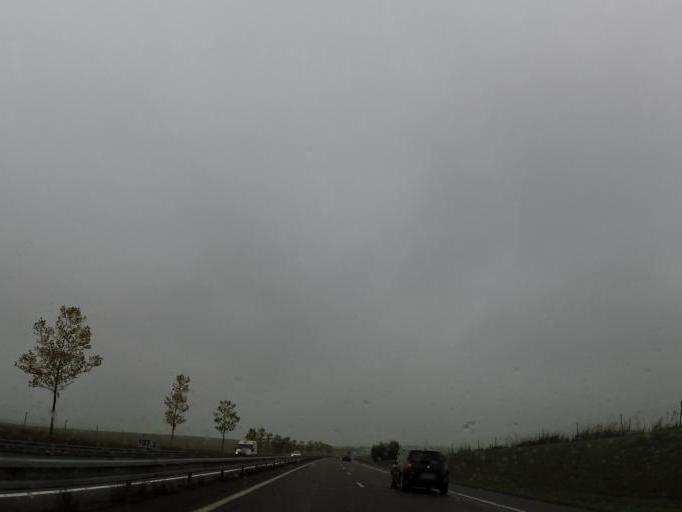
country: FR
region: Champagne-Ardenne
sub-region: Departement de la Marne
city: Suippes
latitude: 49.0506
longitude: 4.6732
